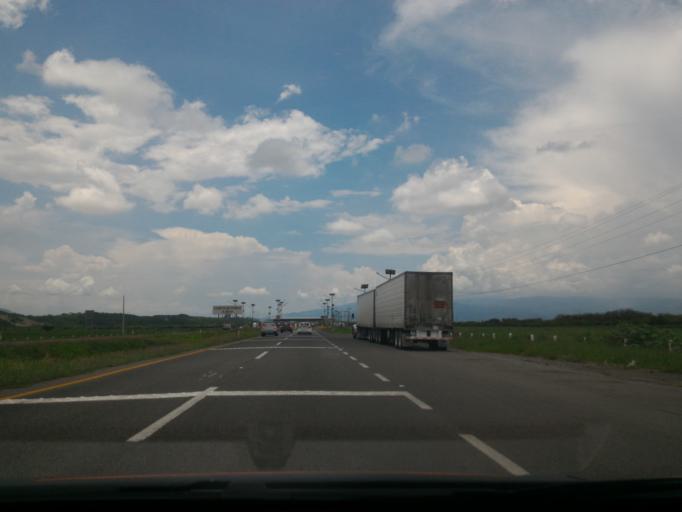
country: MX
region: Jalisco
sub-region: Acatlan de Juarez
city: Villa de los Ninos
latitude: 20.3786
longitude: -103.5764
